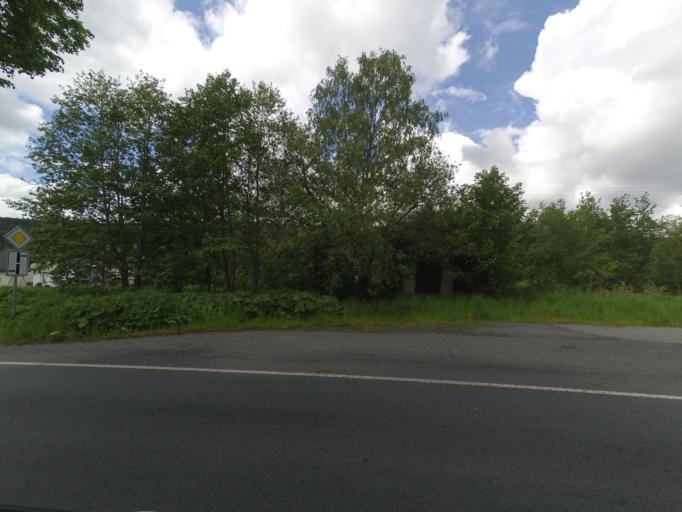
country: CZ
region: Plzensky
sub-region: Okres Klatovy
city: Zelezna Ruda
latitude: 49.1536
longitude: 13.2255
